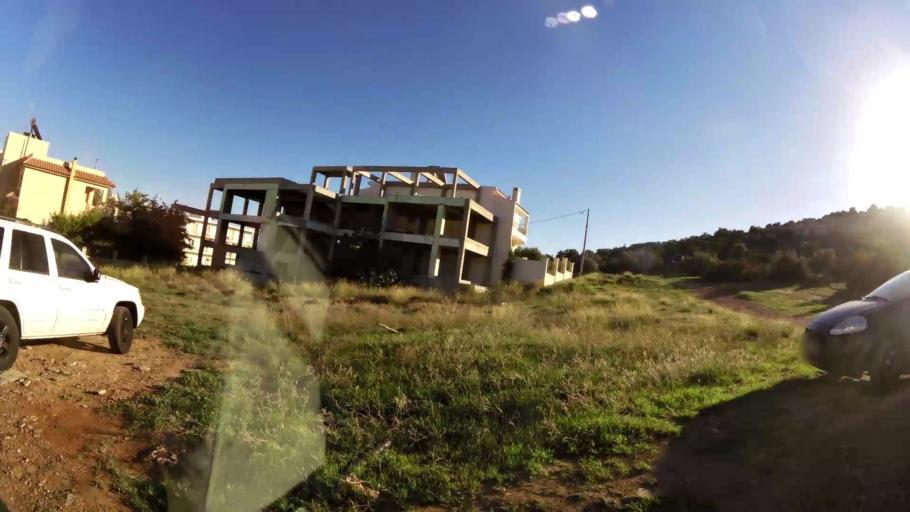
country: GR
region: Attica
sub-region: Nomarchia Anatolikis Attikis
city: Vari
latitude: 37.8312
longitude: 23.7998
